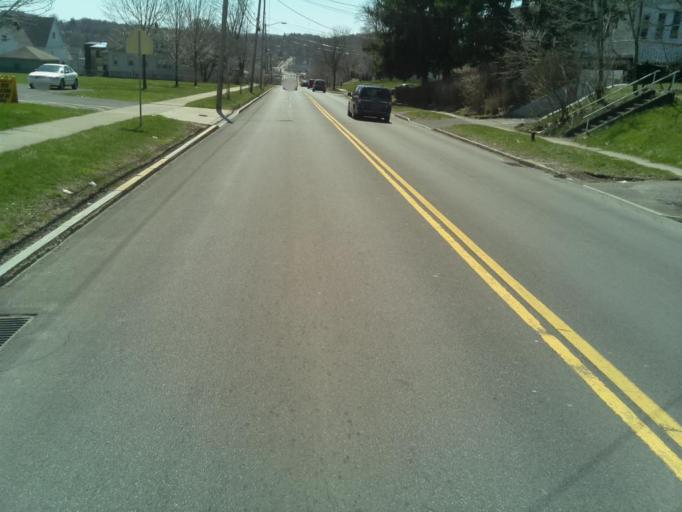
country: US
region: New York
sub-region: Onondaga County
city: Lyncourt
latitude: 43.0580
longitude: -76.1219
